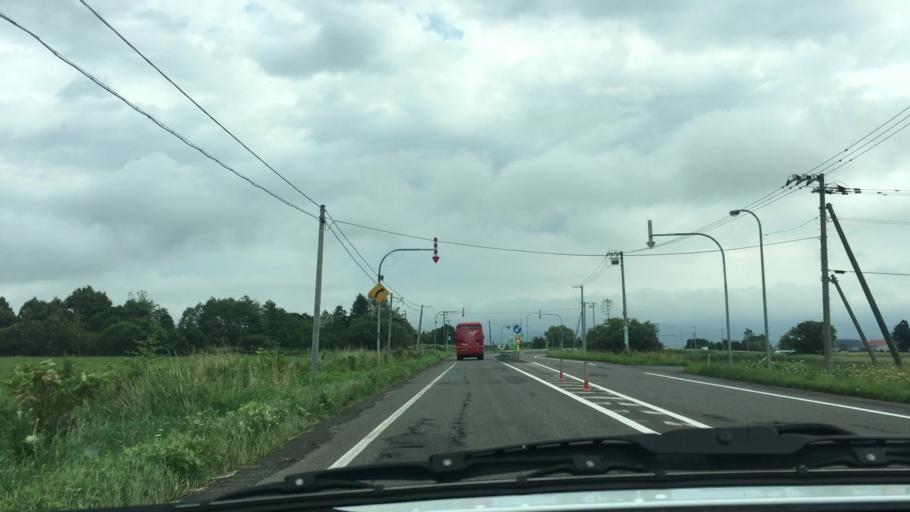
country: JP
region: Hokkaido
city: Chitose
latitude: 42.9453
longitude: 141.7659
